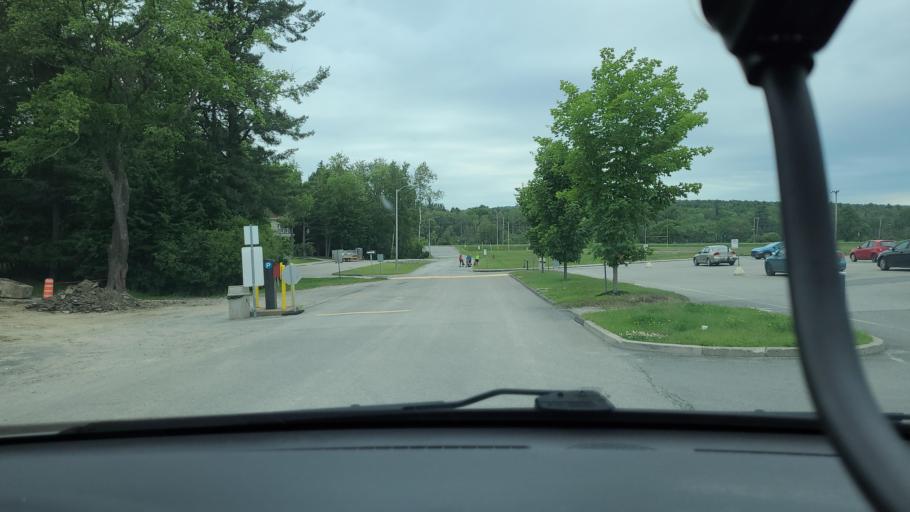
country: CA
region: Quebec
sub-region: Estrie
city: Sherbrooke
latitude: 45.3642
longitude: -71.8432
